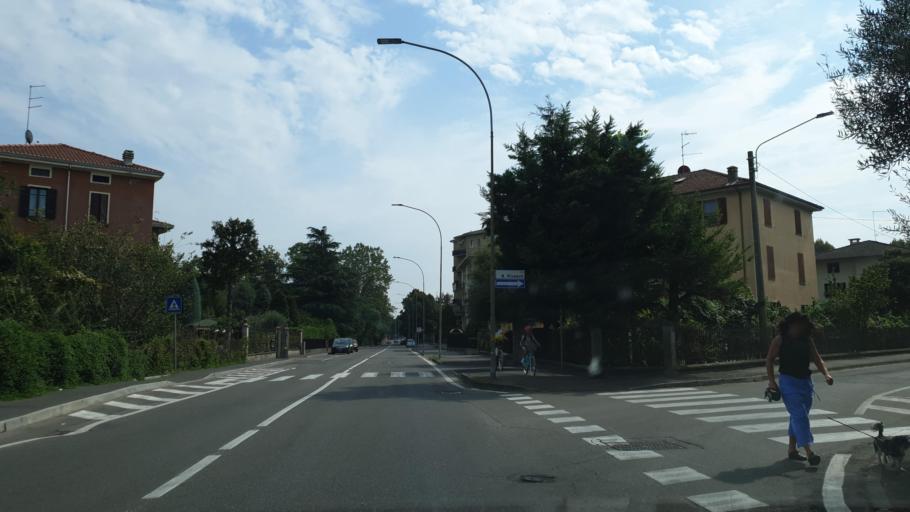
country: IT
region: Emilia-Romagna
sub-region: Provincia di Parma
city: Parma
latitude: 44.8106
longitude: 10.2943
